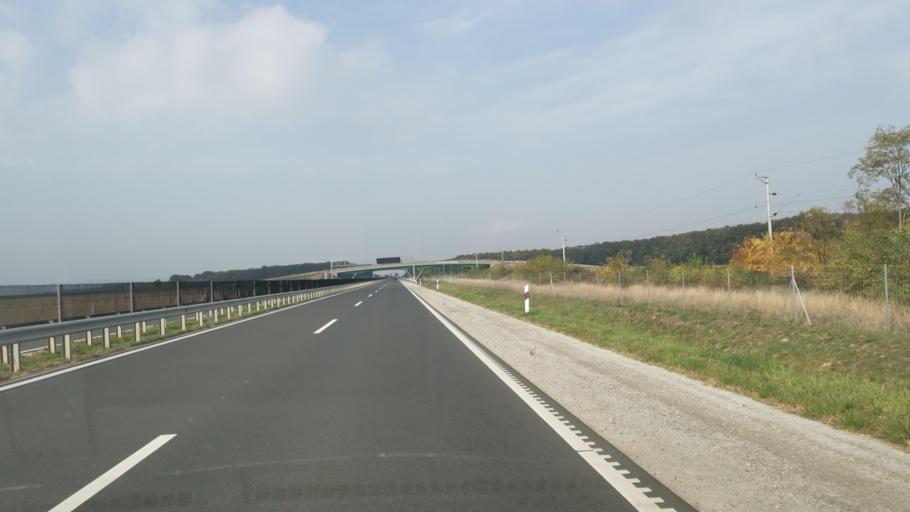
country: AT
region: Burgenland
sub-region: Politischer Bezirk Oberpullendorf
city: Deutschkreutz
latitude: 47.6144
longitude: 16.6626
